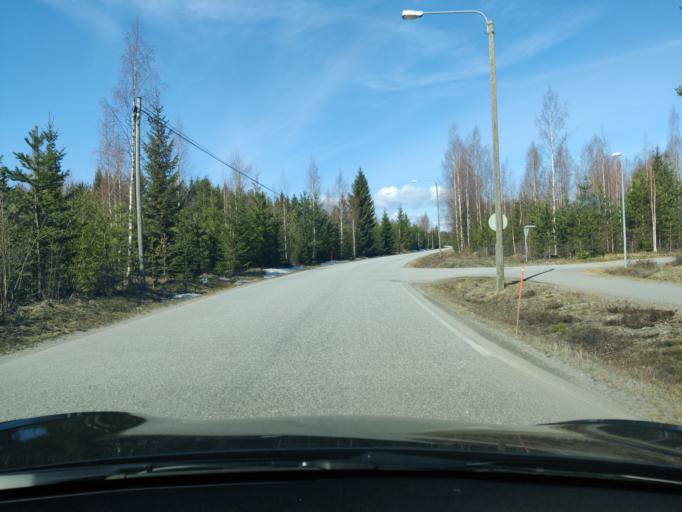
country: FI
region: Northern Savo
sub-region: Kuopio
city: Vehmersalmi
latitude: 62.7688
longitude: 27.9886
